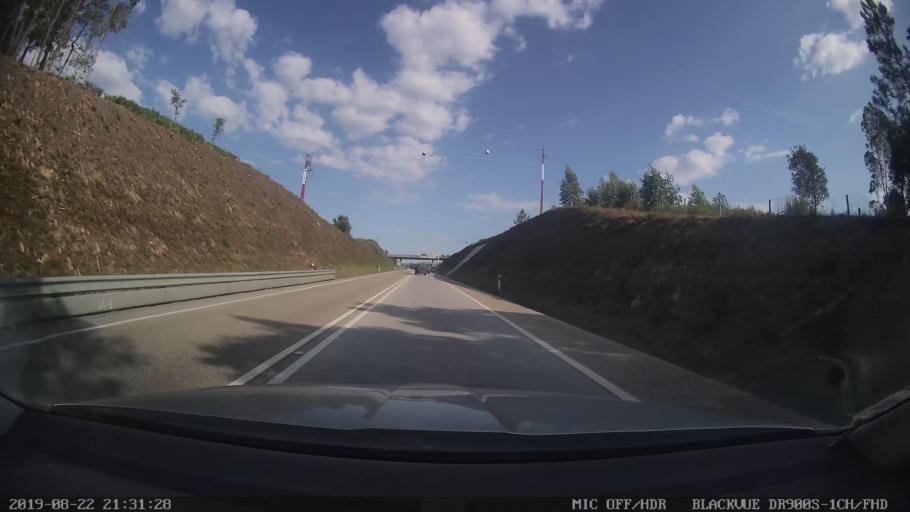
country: PT
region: Leiria
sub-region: Pedrogao Grande
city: Pedrogao Grande
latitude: 39.9205
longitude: -8.1545
